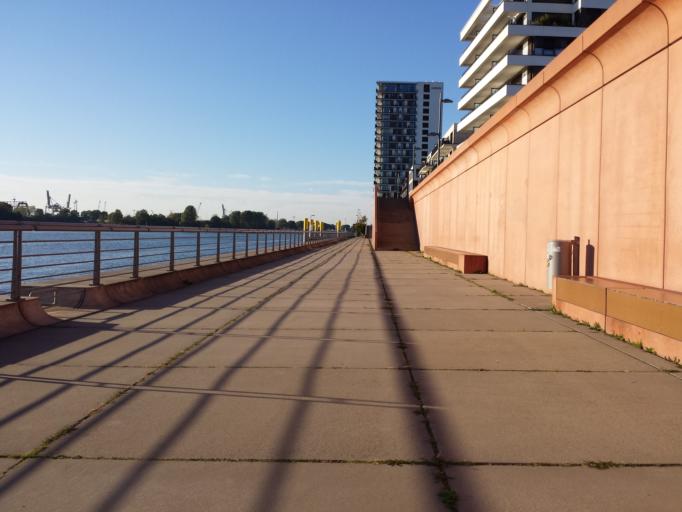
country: DE
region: Bremen
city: Bremen
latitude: 53.0957
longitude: 8.7632
